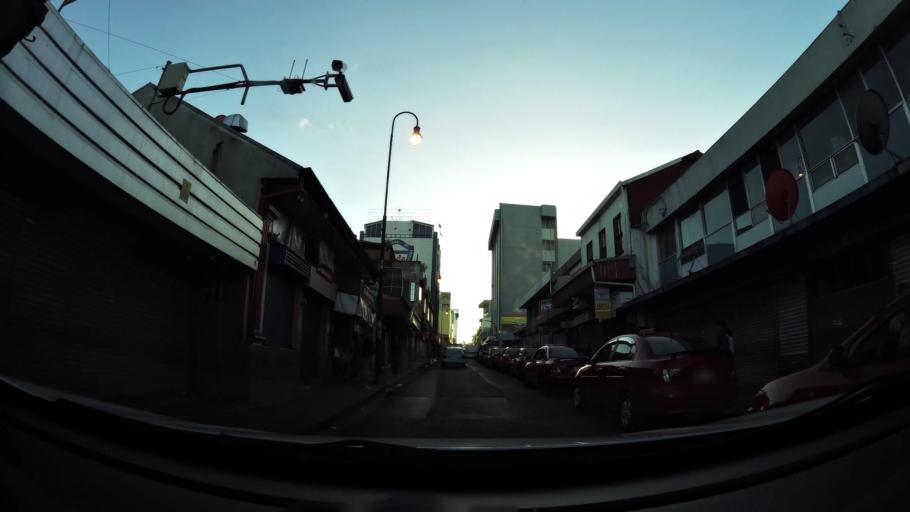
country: CR
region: San Jose
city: San Jose
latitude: 9.9369
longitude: -84.0802
